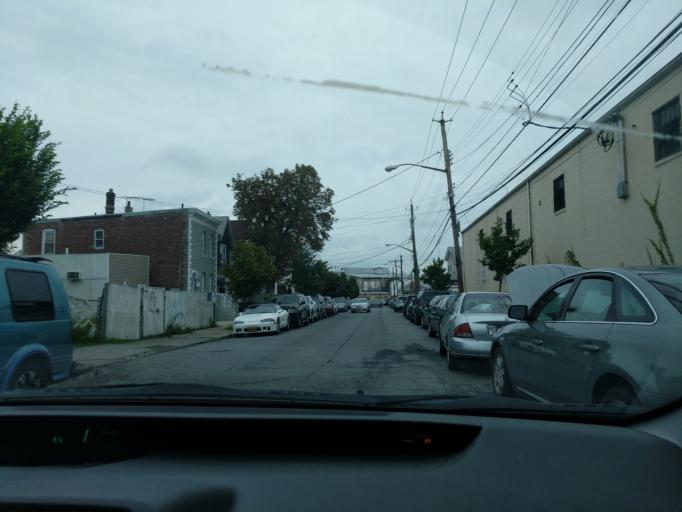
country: US
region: New York
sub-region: Richmond County
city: Bloomfield
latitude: 40.6362
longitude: -74.1474
